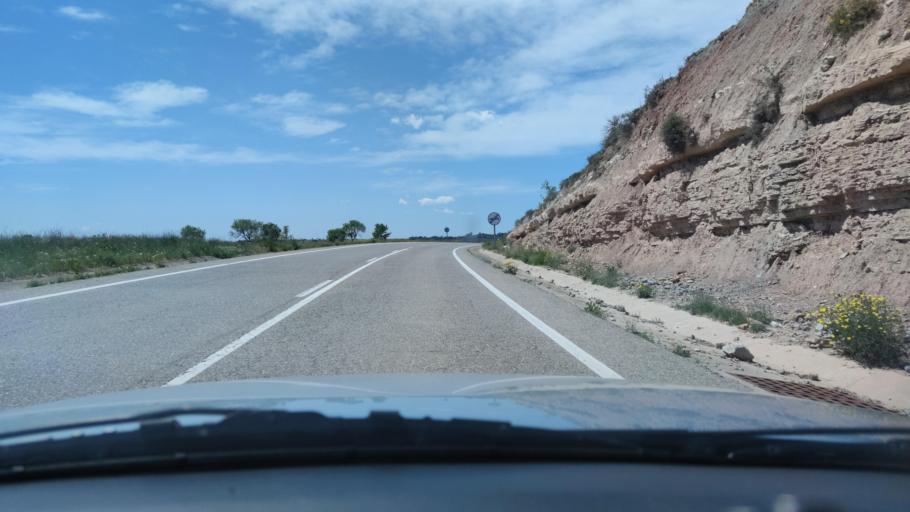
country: ES
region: Catalonia
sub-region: Provincia de Lleida
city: Tora de Riubregos
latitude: 41.7945
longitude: 1.2925
